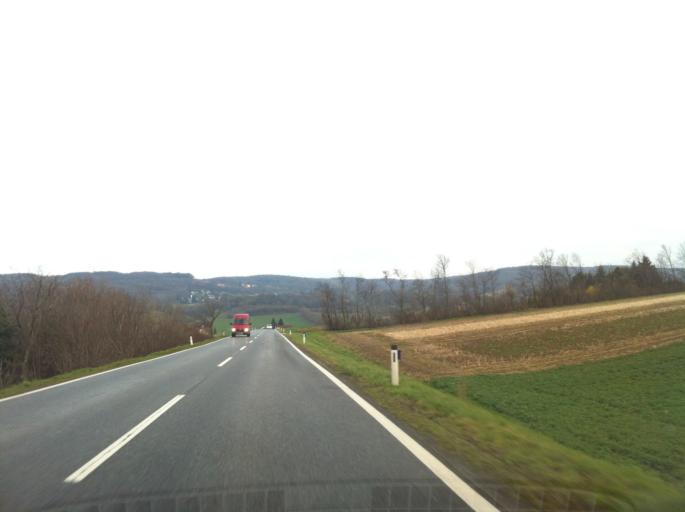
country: AT
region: Lower Austria
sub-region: Politischer Bezirk Tulln
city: Tulbing
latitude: 48.2678
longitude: 16.0742
